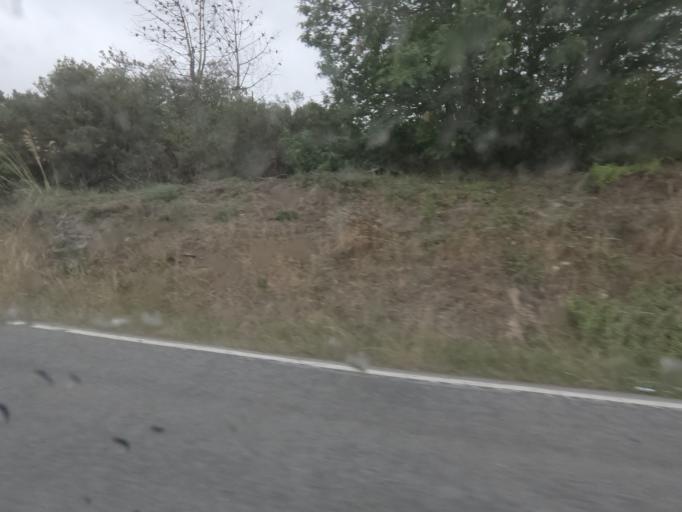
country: PT
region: Vila Real
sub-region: Peso da Regua
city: Peso da Regua
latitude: 41.1308
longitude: -7.7455
